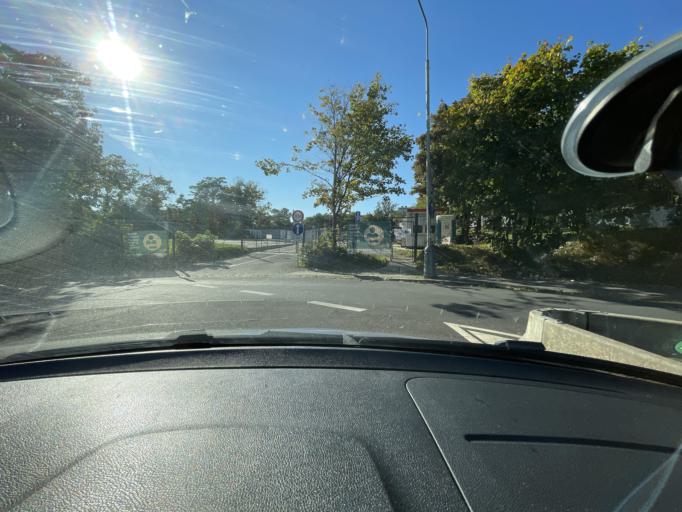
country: CZ
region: Praha
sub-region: Praha 8
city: Liben
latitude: 50.0748
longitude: 14.4839
